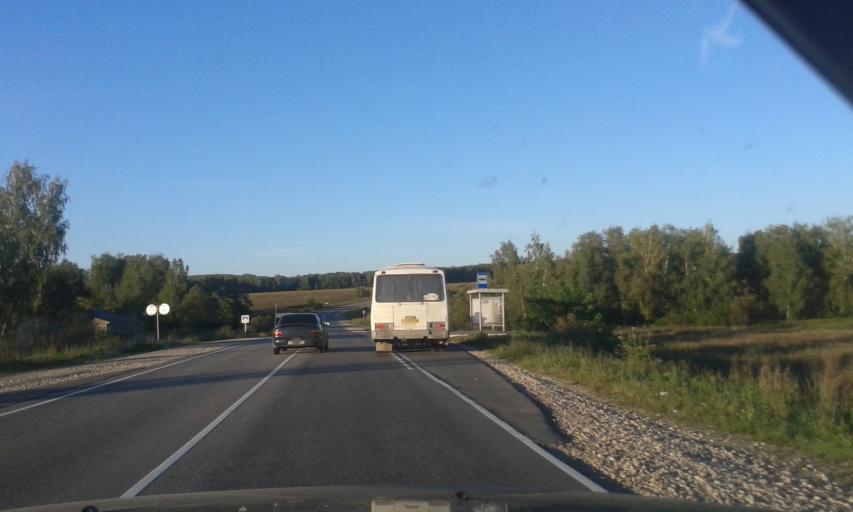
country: RU
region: Tula
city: Krapivna
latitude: 54.1160
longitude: 37.2220
